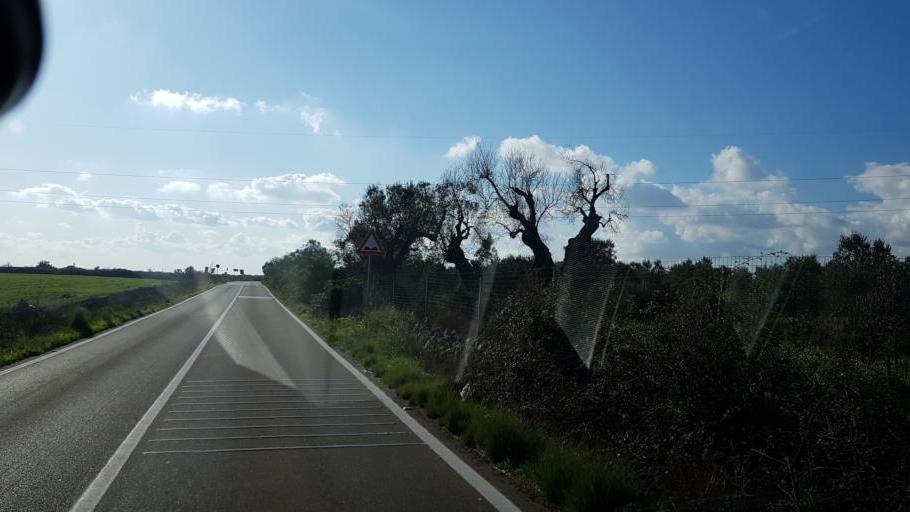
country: IT
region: Apulia
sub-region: Provincia di Lecce
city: Trepuzzi
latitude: 40.4496
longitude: 18.1081
